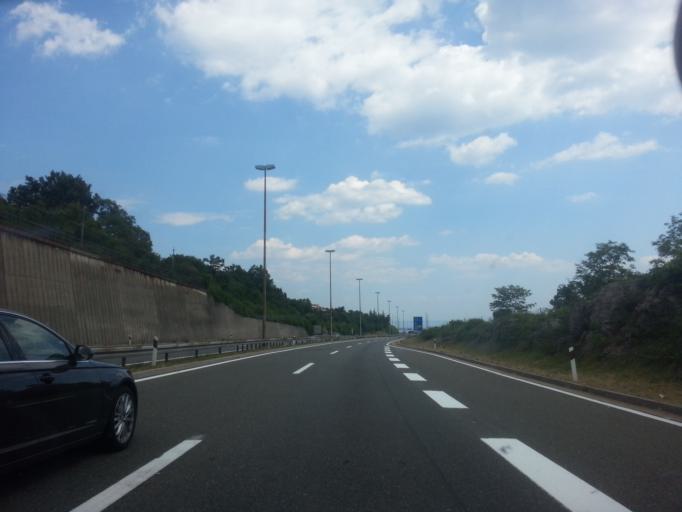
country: HR
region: Primorsko-Goranska
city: Rubesi
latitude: 45.3540
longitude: 14.3563
